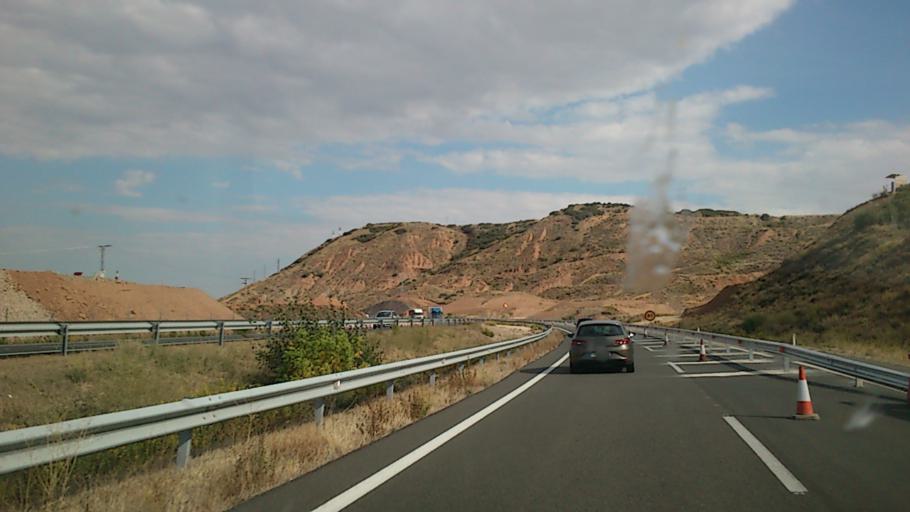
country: ES
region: La Rioja
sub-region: Provincia de La Rioja
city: Murillo de Rio Leza
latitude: 42.4468
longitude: -2.3439
